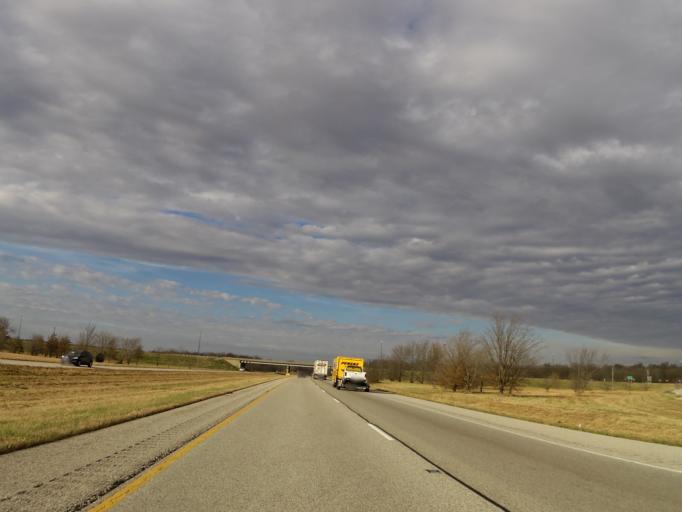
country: US
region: Illinois
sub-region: Washington County
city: Nashville
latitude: 38.3915
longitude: -89.3674
